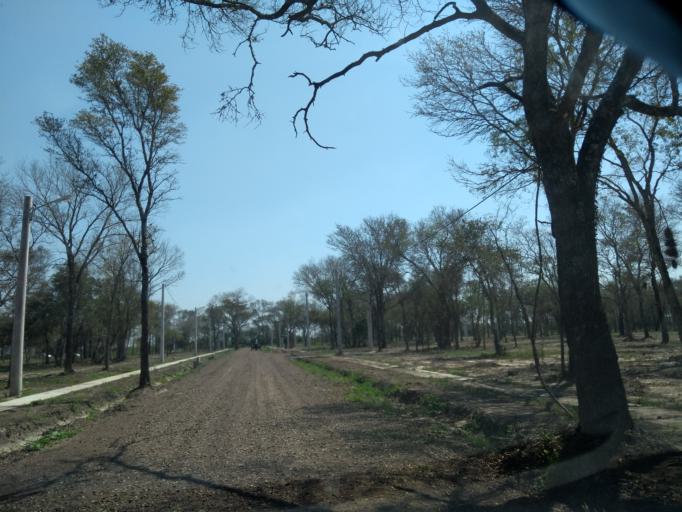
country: AR
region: Chaco
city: Resistencia
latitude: -27.4124
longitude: -58.9550
